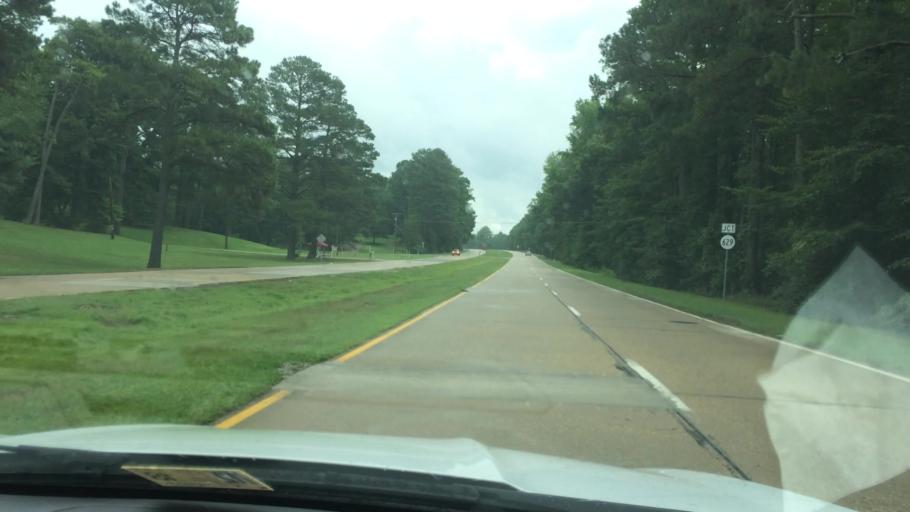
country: US
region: Virginia
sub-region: New Kent County
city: New Kent
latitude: 37.4402
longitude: -77.0300
